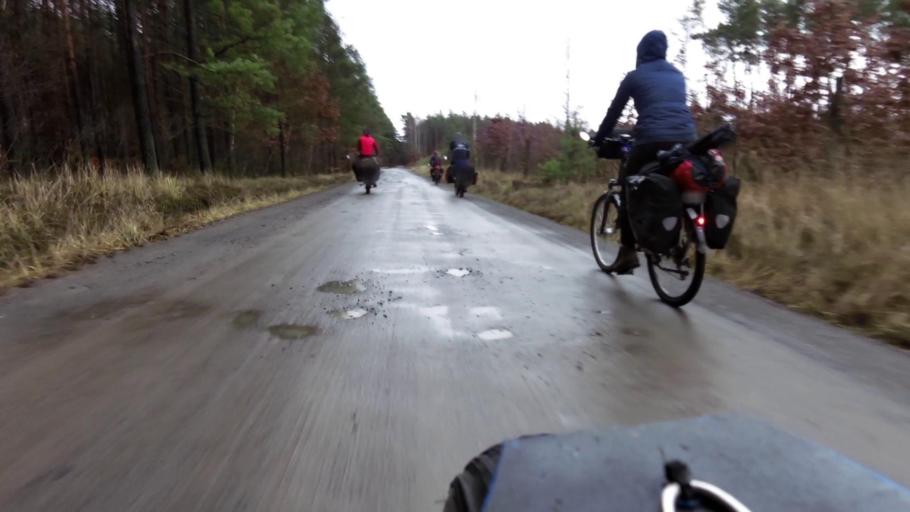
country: PL
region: Lubusz
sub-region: Powiat gorzowski
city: Witnica
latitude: 52.6994
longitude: 14.8394
